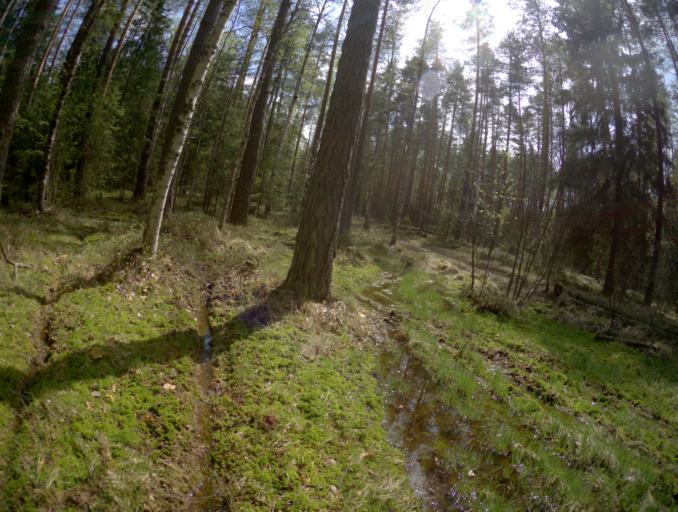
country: RU
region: Vladimir
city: Golovino
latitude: 55.8932
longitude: 40.3873
